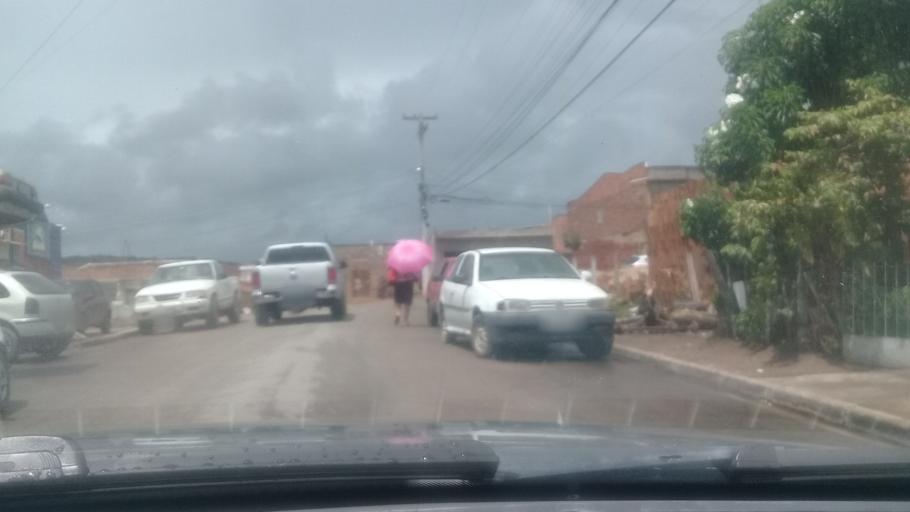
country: BR
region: Pernambuco
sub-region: Vitoria De Santo Antao
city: Vitoria de Santo Antao
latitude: -8.1273
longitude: -35.2882
